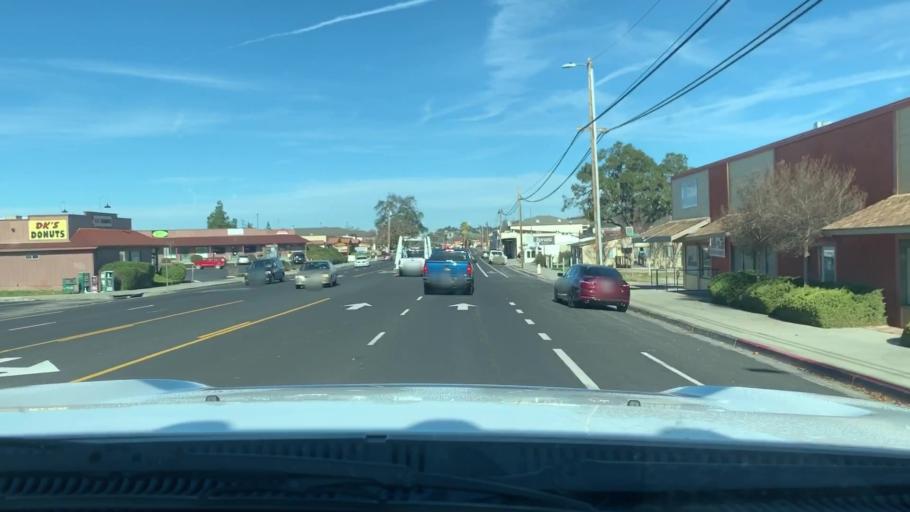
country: US
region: California
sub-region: San Luis Obispo County
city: Atascadero
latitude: 35.4723
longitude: -120.6535
